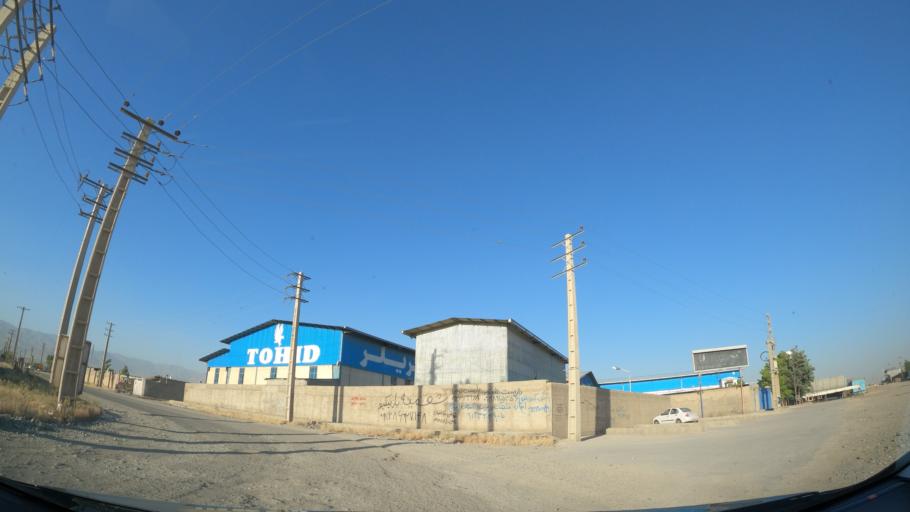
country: IR
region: Alborz
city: Hashtgerd
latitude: 35.9166
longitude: 50.7588
